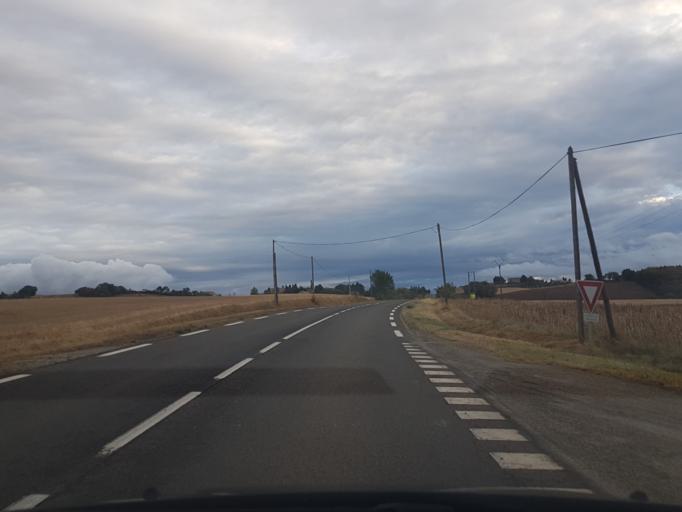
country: FR
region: Midi-Pyrenees
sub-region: Departement de l'Ariege
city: Mirepoix
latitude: 43.1360
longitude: 1.9536
